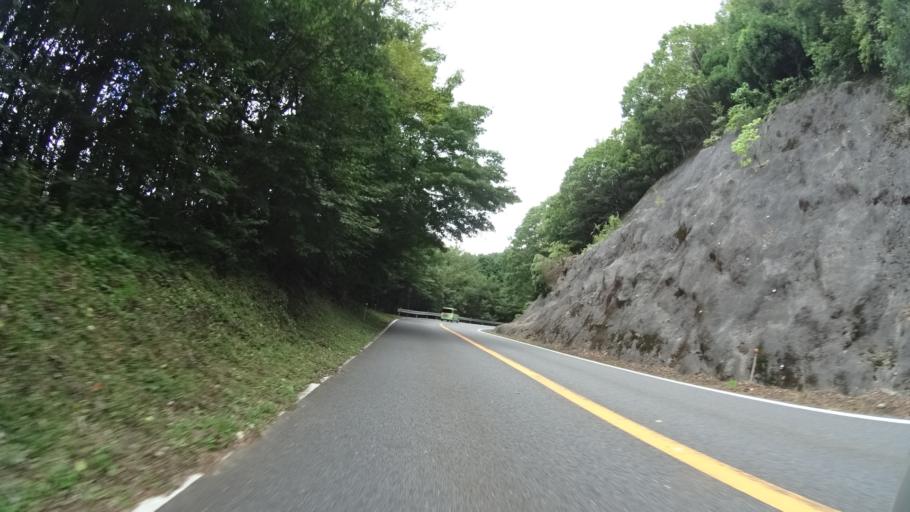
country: JP
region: Oita
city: Tsukawaki
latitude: 33.1934
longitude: 131.2843
